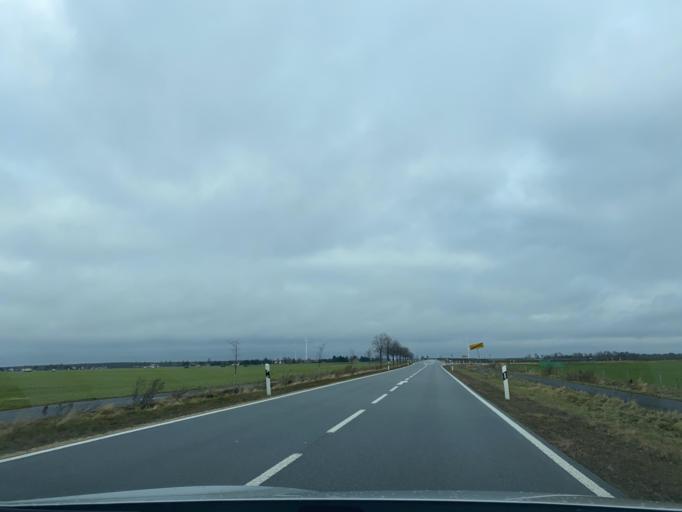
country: PL
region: Lower Silesian Voivodeship
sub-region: Powiat zgorzelecki
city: Piensk
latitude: 51.2322
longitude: 14.9772
